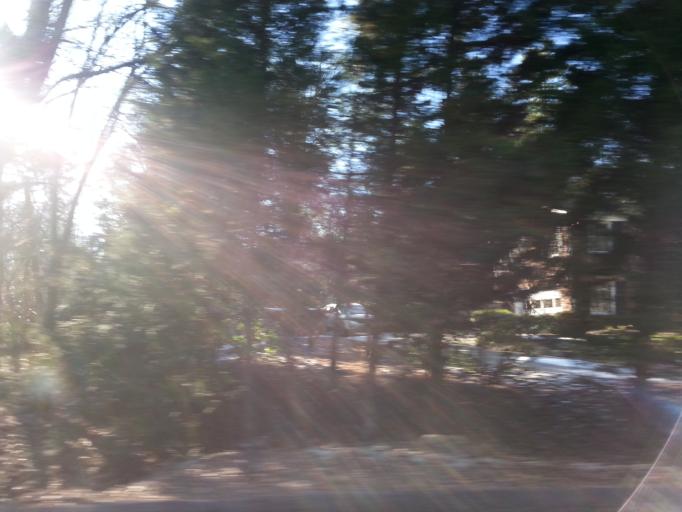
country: US
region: Tennessee
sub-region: Knox County
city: Knoxville
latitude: 35.8934
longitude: -83.9759
